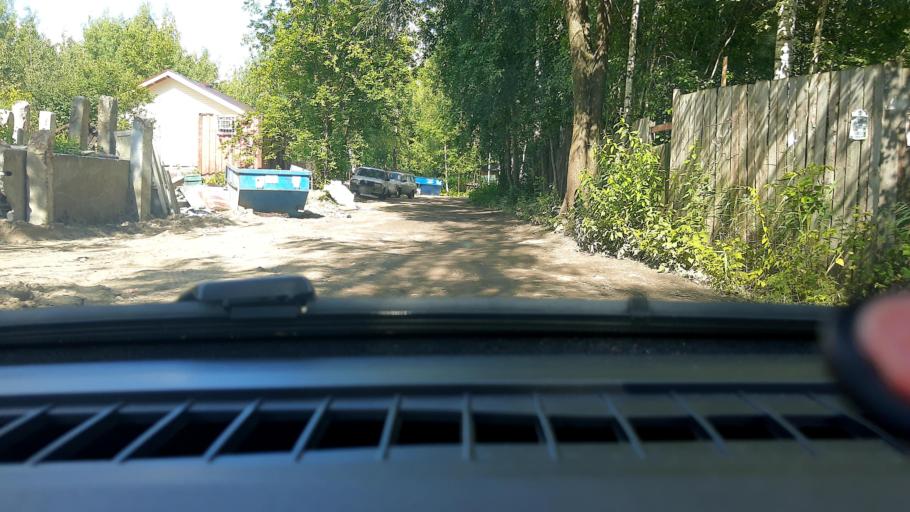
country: RU
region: Nizjnij Novgorod
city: Gorbatovka
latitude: 56.3238
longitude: 43.8316
